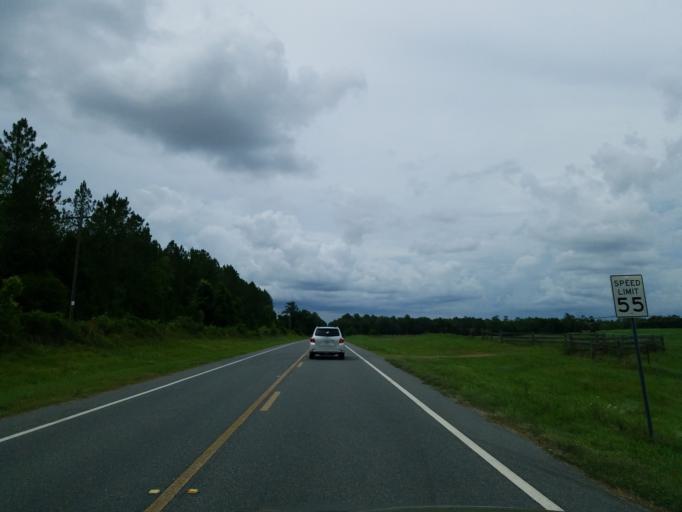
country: US
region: Florida
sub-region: Alachua County
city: High Springs
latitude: 29.9313
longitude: -82.5061
